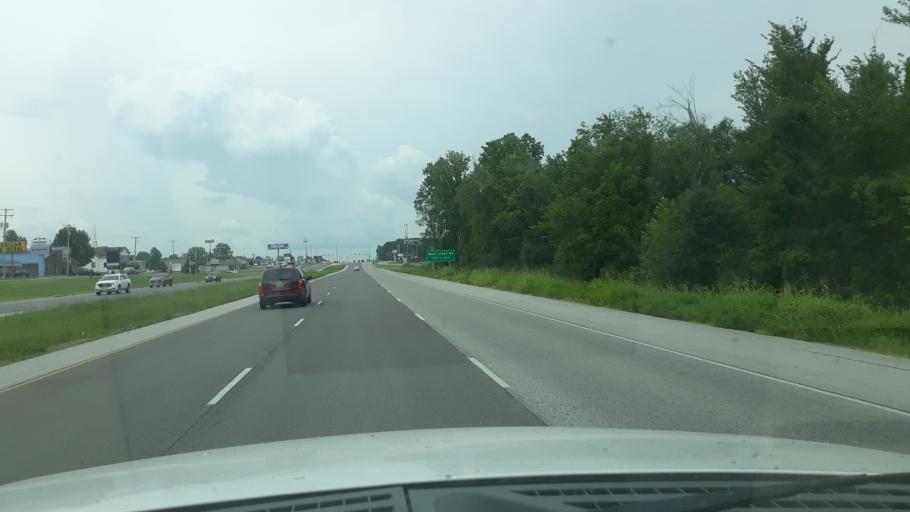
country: US
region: Illinois
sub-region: Williamson County
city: Carterville
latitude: 37.7449
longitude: -89.0847
